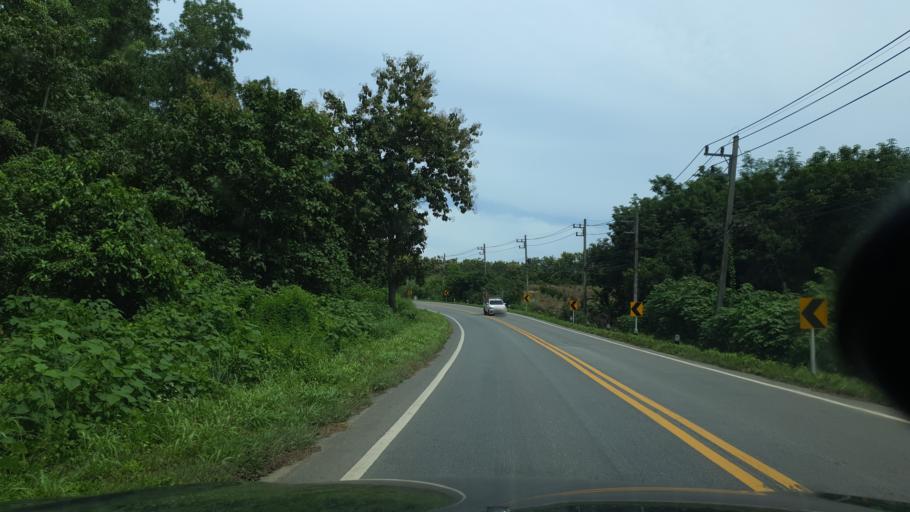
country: TH
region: Sukhothai
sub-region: Amphoe Si Satchanalai
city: Si Satchanalai
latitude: 17.6446
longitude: 99.6867
